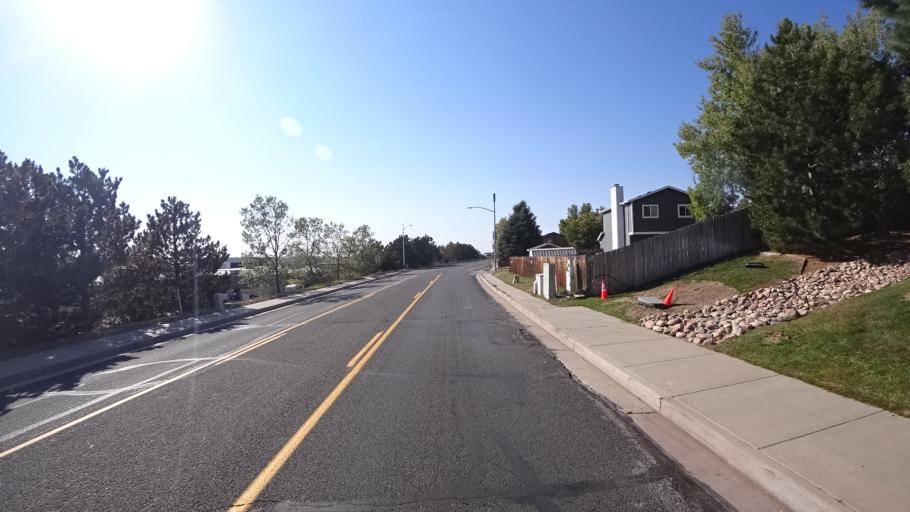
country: US
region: Colorado
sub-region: El Paso County
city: Cimarron Hills
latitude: 38.8760
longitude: -104.7234
